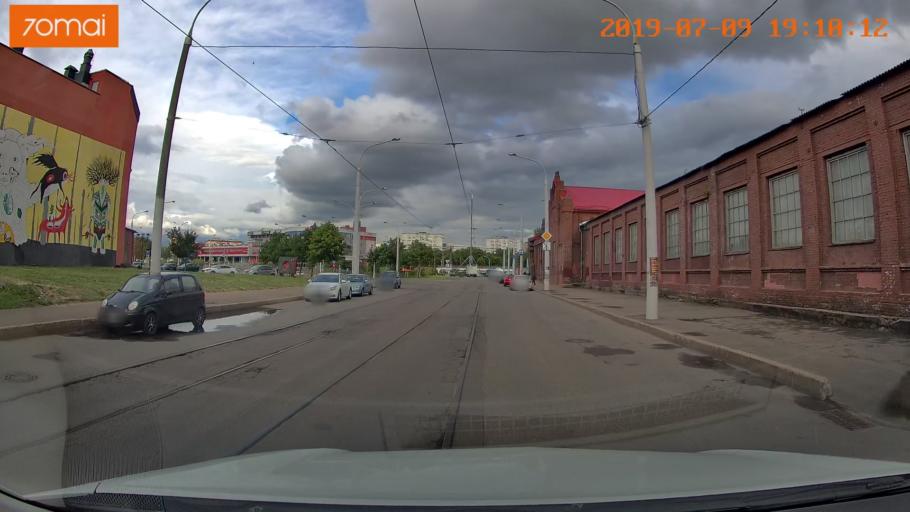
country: BY
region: Minsk
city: Minsk
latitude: 53.8892
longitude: 27.5767
